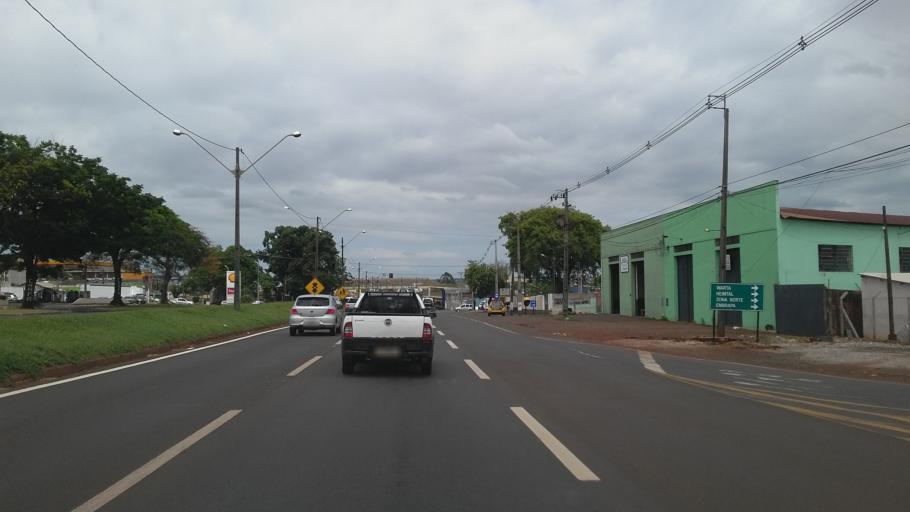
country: BR
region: Parana
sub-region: Londrina
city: Londrina
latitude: -23.2929
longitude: -51.1412
